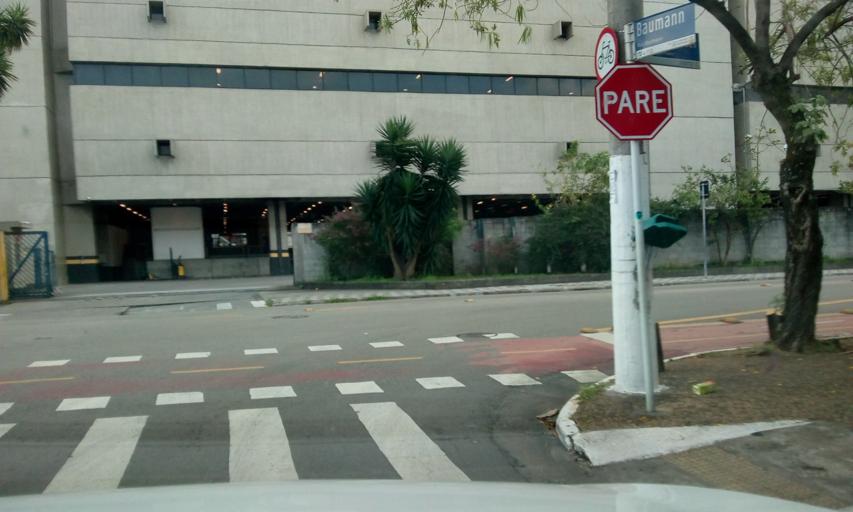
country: BR
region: Sao Paulo
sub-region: Osasco
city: Osasco
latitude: -23.5285
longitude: -46.7372
